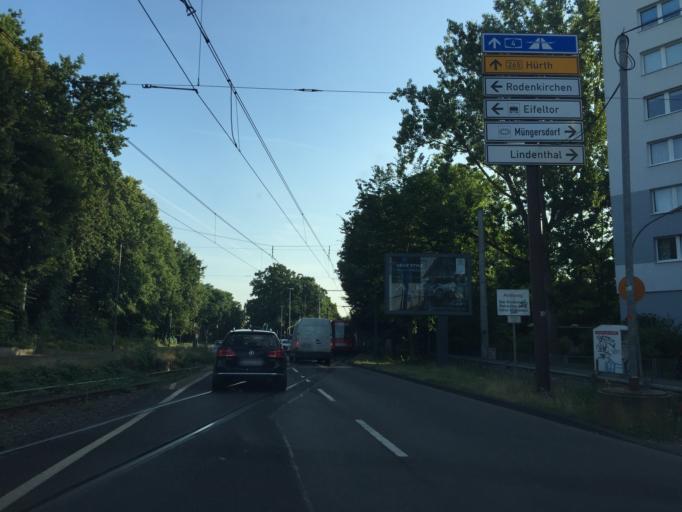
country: DE
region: North Rhine-Westphalia
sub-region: Regierungsbezirk Koln
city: Neustadt/Sued
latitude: 50.9056
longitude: 6.9168
